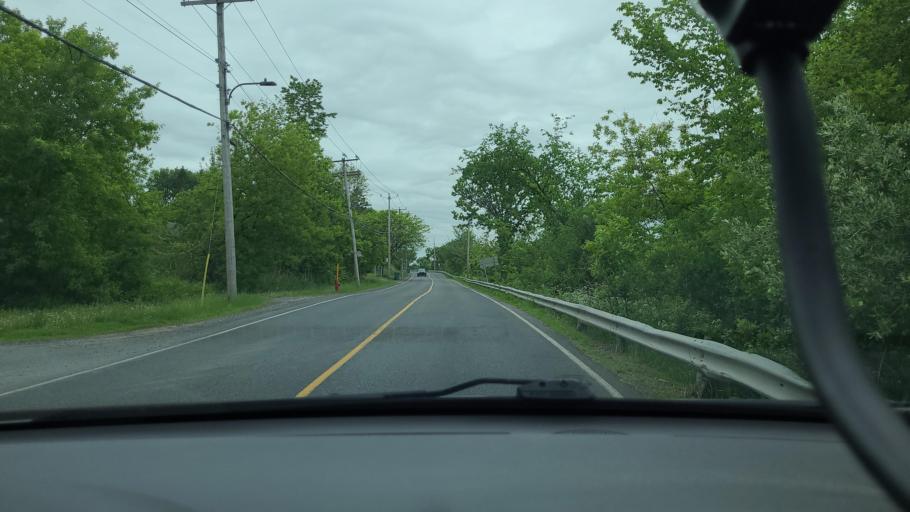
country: CA
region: Quebec
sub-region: Lanaudiere
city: Charlemagne
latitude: 45.6971
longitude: -73.5155
